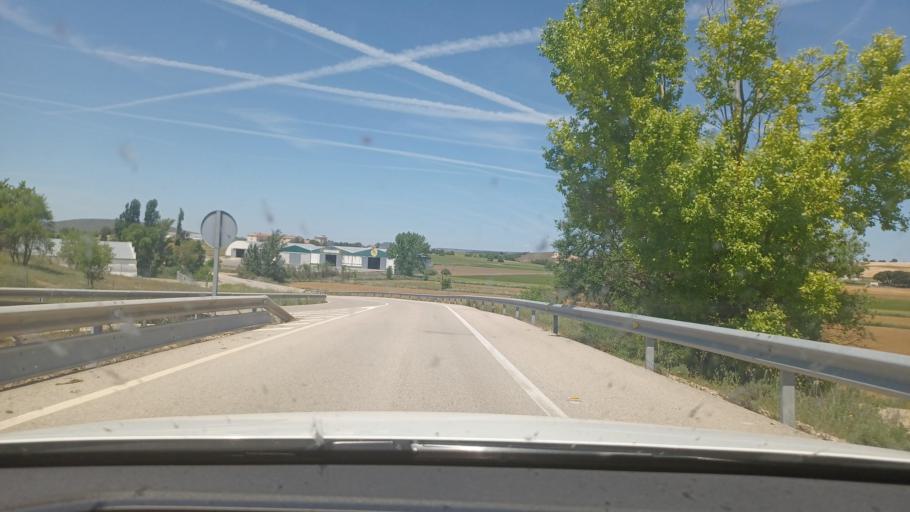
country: ES
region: Castille-La Mancha
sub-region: Provincia de Cuenca
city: Villares del Saz
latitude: 39.8341
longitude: -2.4949
